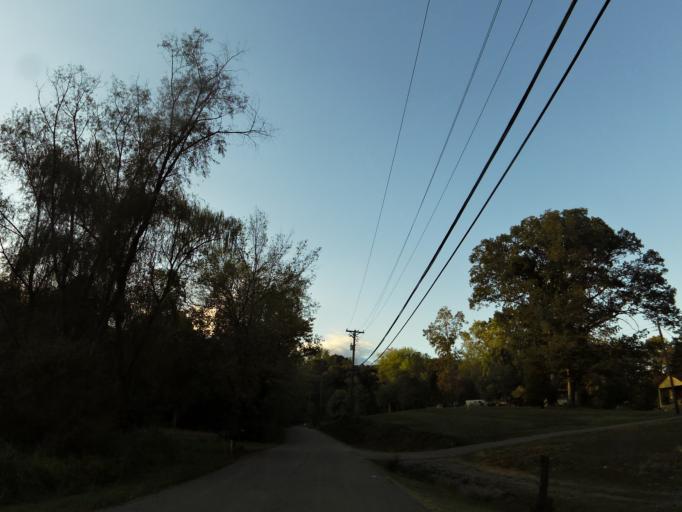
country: US
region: Tennessee
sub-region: Knox County
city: Knoxville
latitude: 35.9087
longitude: -83.9436
